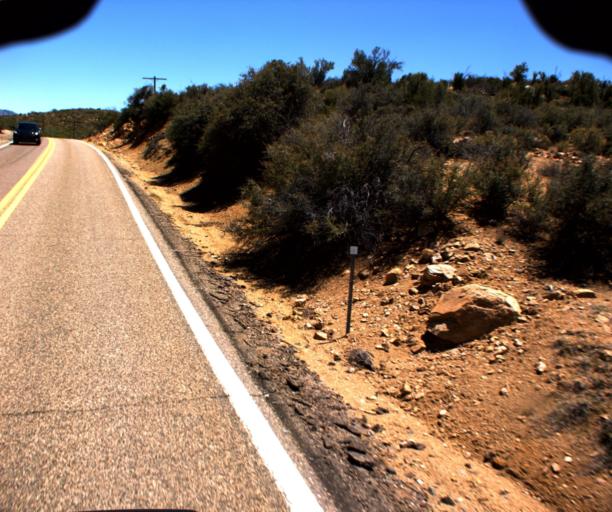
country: US
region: Arizona
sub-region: Yavapai County
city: Bagdad
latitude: 34.4428
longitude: -112.9367
